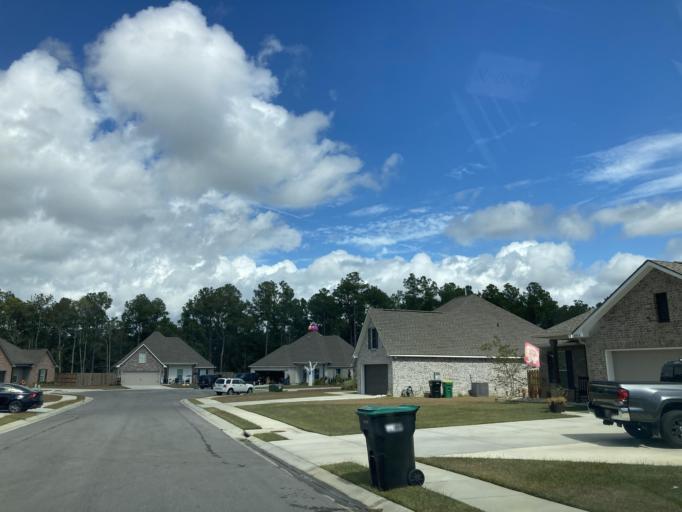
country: US
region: Mississippi
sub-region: Jackson County
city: Gulf Hills
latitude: 30.4526
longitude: -88.8296
